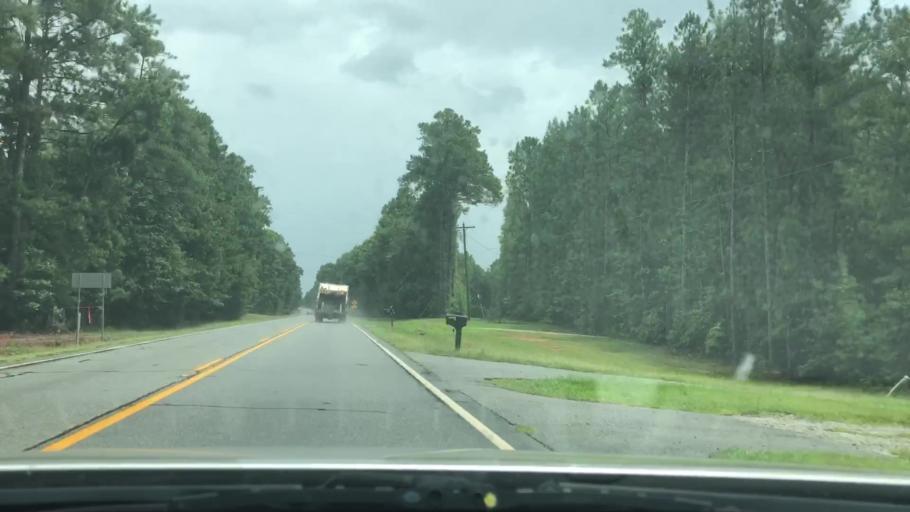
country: US
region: Georgia
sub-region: Pike County
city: Zebulon
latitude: 33.0779
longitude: -84.2537
